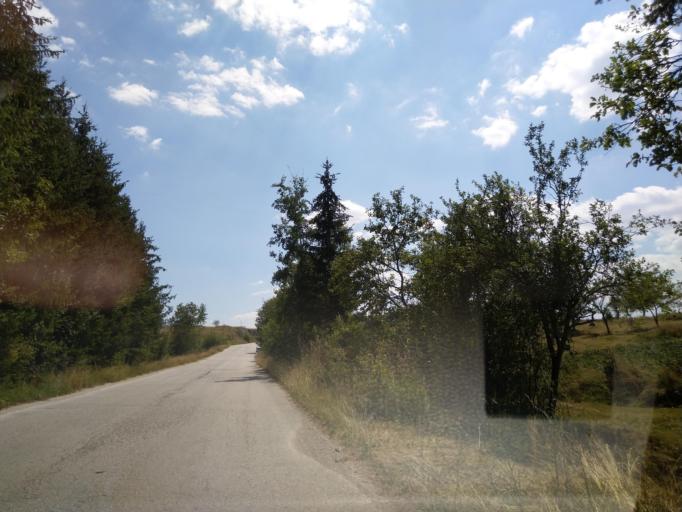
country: RS
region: Central Serbia
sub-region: Zlatiborski Okrug
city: Nova Varos
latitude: 43.4324
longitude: 19.9499
